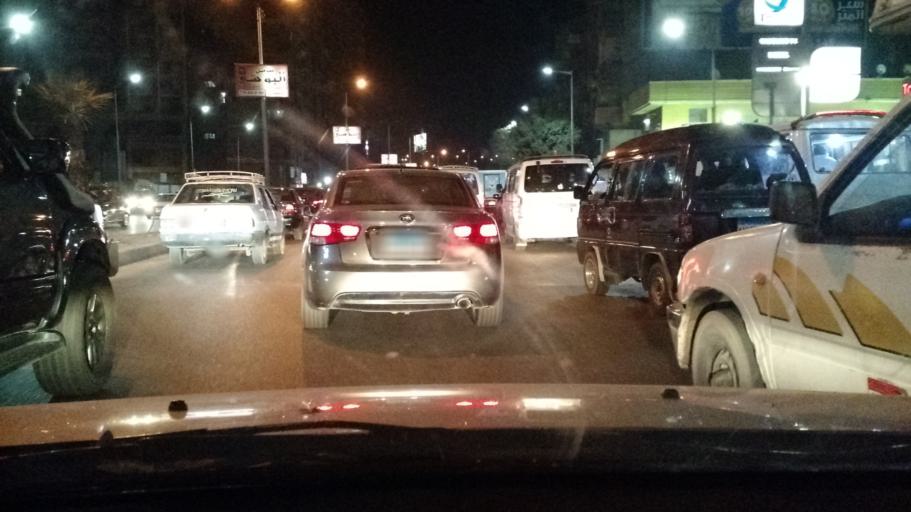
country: EG
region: Al Jizah
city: Al Jizah
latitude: 29.9907
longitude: 31.2153
